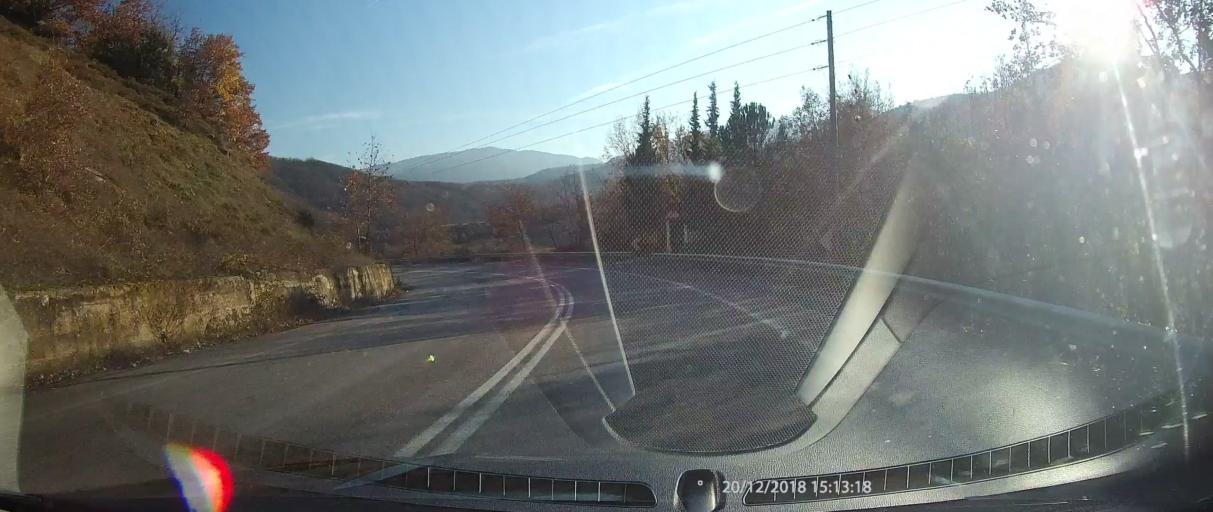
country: GR
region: Central Greece
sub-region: Nomos Fthiotidos
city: Makrakomi
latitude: 38.9339
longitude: 21.9657
